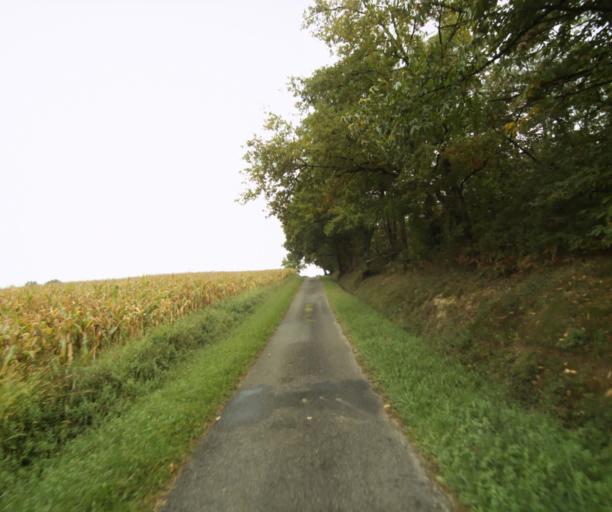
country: FR
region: Midi-Pyrenees
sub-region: Departement du Gers
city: Cazaubon
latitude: 43.9264
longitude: -0.1376
